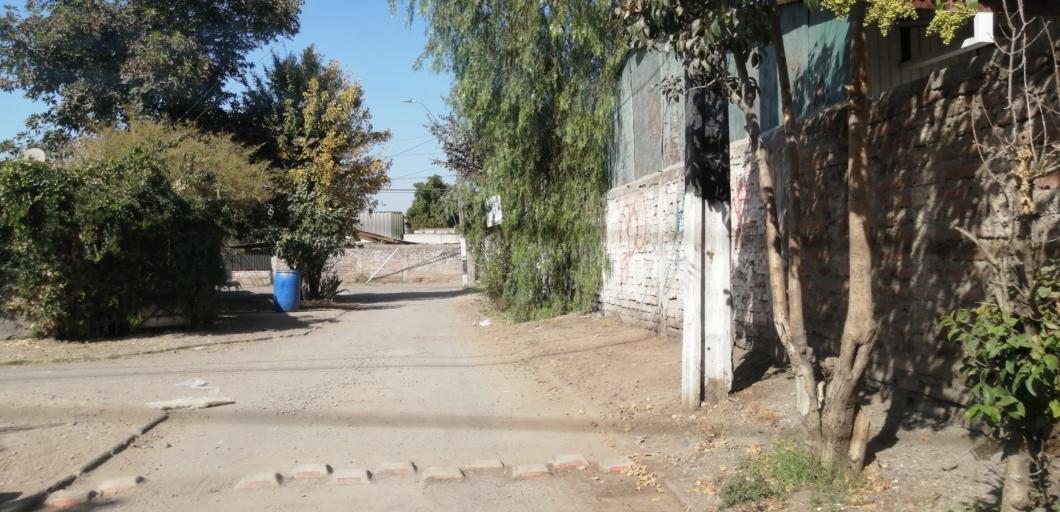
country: CL
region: Santiago Metropolitan
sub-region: Provincia de Santiago
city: Lo Prado
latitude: -33.4369
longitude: -70.7447
